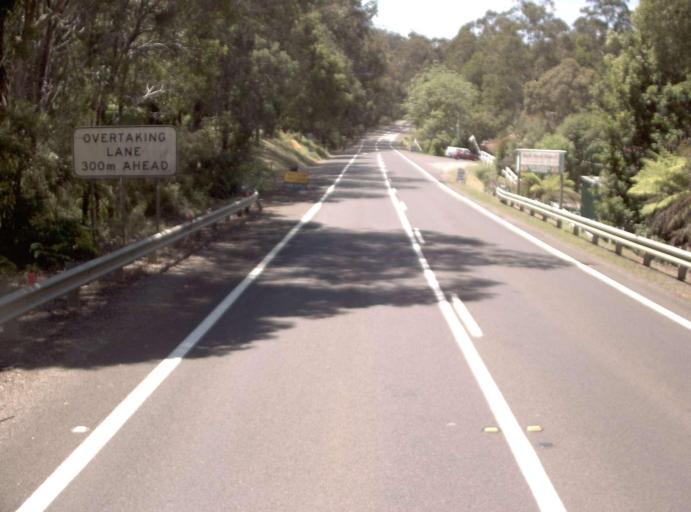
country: AU
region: New South Wales
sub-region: Bombala
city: Bombala
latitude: -37.6531
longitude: 148.8161
